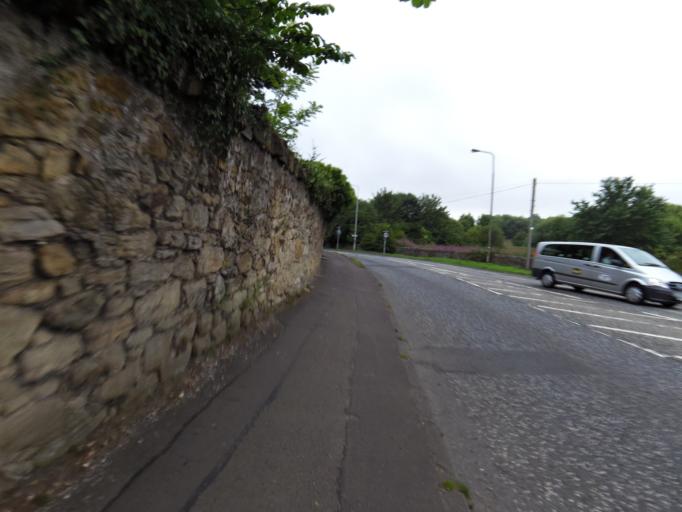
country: GB
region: Scotland
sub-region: Midlothian
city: Bonnyrigg
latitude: 55.9131
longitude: -3.1252
